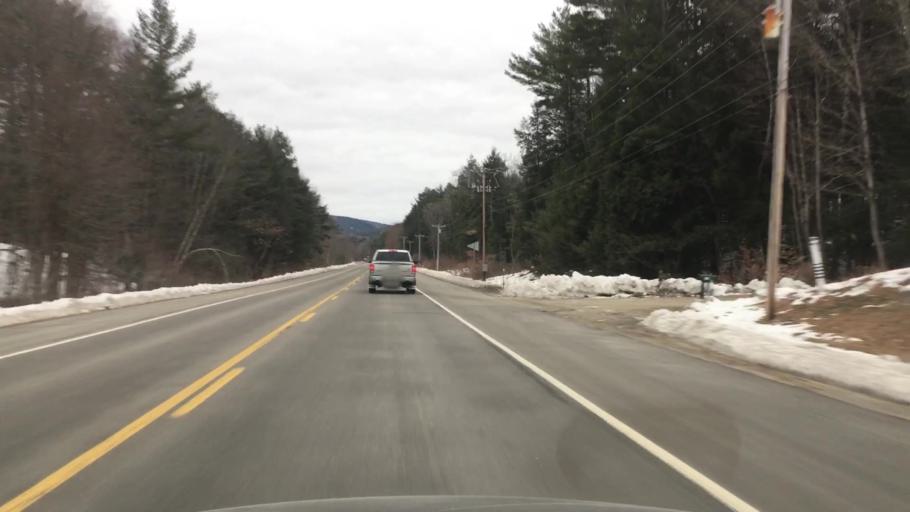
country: US
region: New Hampshire
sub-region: Merrimack County
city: Newbury
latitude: 43.2977
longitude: -71.9979
